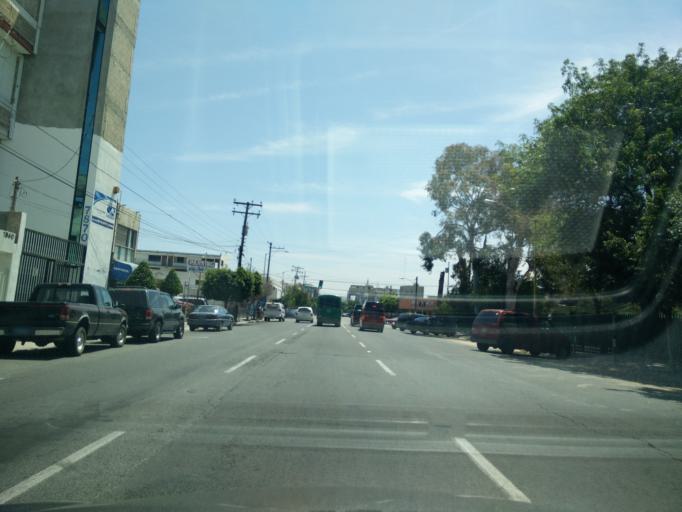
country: MX
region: Baja California
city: Tijuana
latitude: 32.5323
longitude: -117.0423
